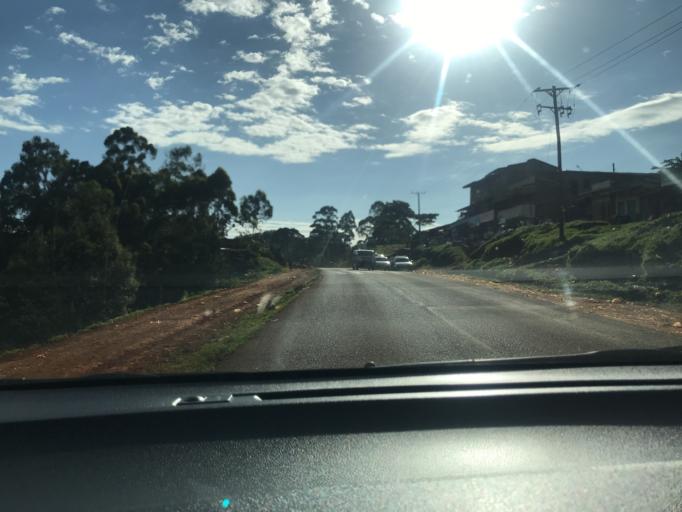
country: KE
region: Kirinyaga
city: Keruguya
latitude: -0.4796
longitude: 37.1794
